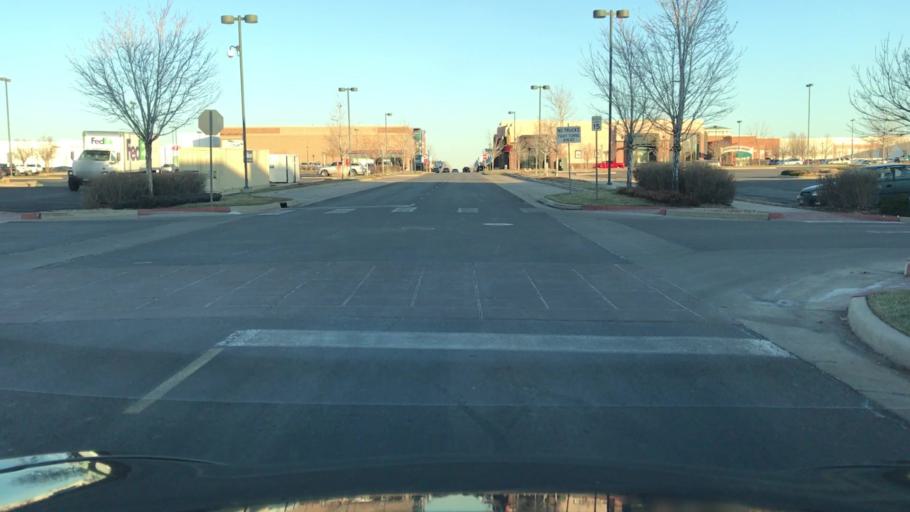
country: US
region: Colorado
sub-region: Adams County
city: Commerce City
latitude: 39.7824
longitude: -104.8951
